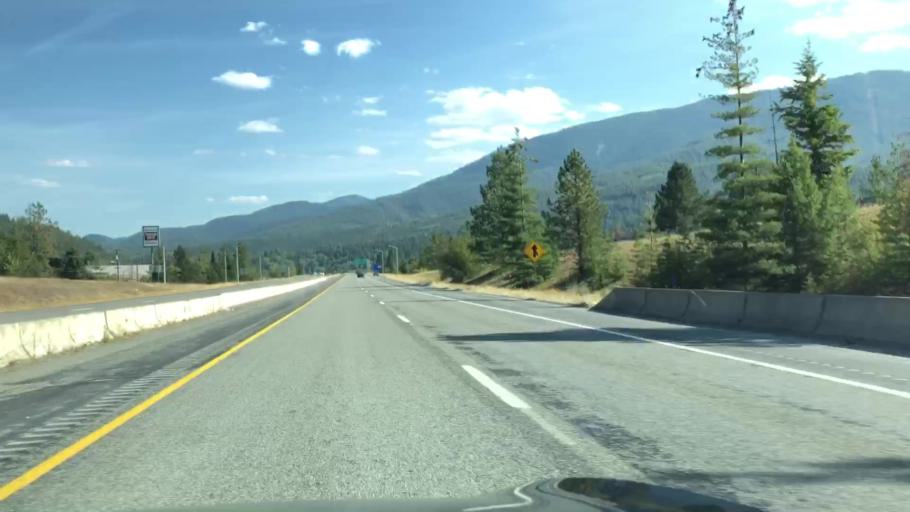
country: US
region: Idaho
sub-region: Shoshone County
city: Kellogg
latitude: 47.5453
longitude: -116.1323
